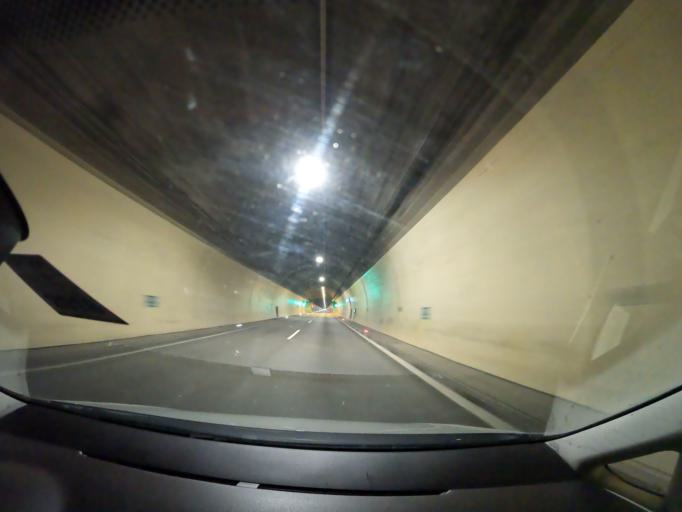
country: AT
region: Carinthia
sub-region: Politischer Bezirk Wolfsberg
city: Bad Sankt Leonhard im Lavanttal
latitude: 46.9084
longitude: 14.8233
